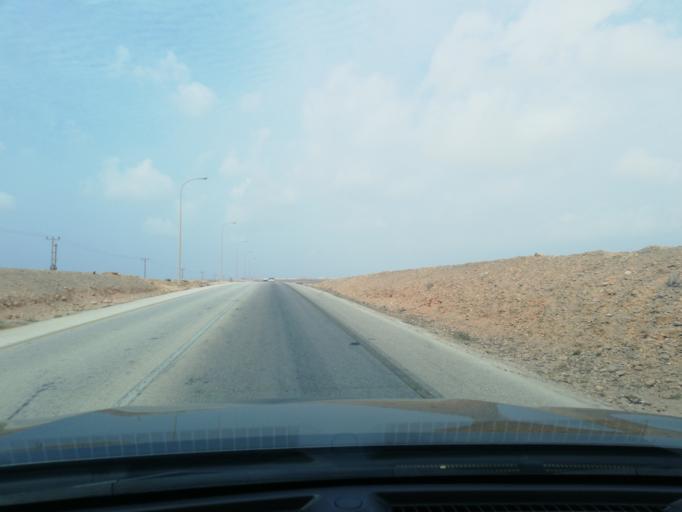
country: OM
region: Zufar
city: Salalah
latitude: 16.9528
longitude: 53.8596
